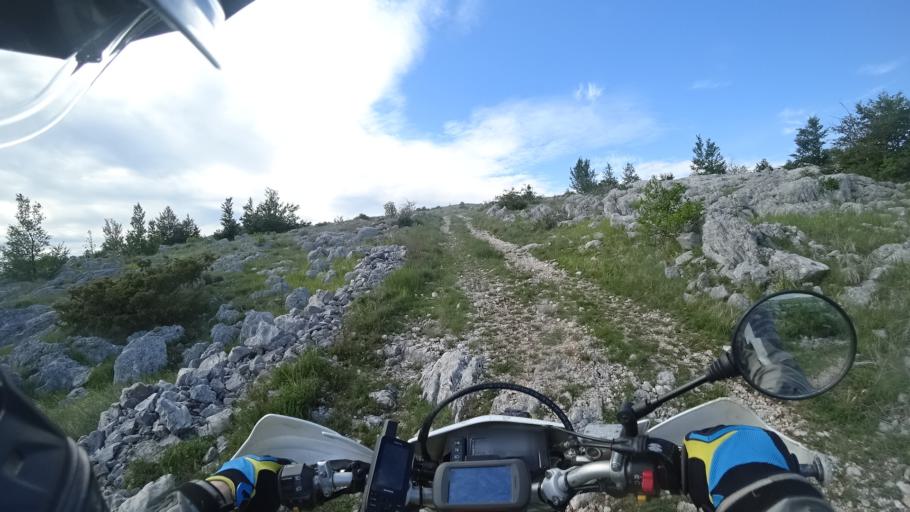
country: HR
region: Splitsko-Dalmatinska
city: Hrvace
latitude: 43.8025
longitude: 16.4315
